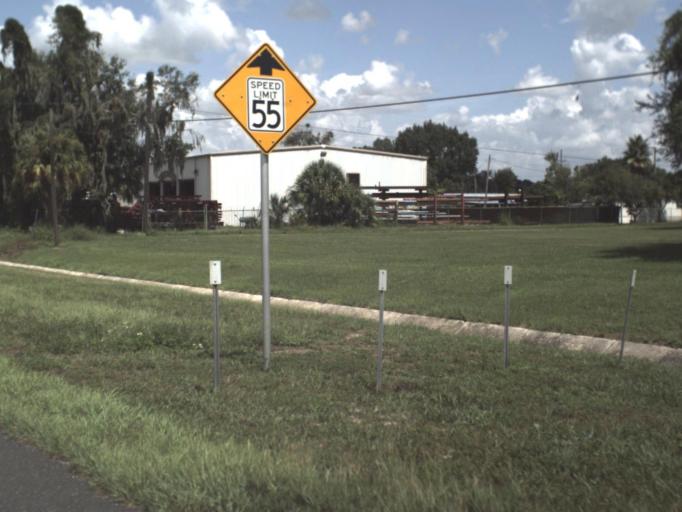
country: US
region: Florida
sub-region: Polk County
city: Bartow
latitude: 27.8582
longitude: -81.8282
